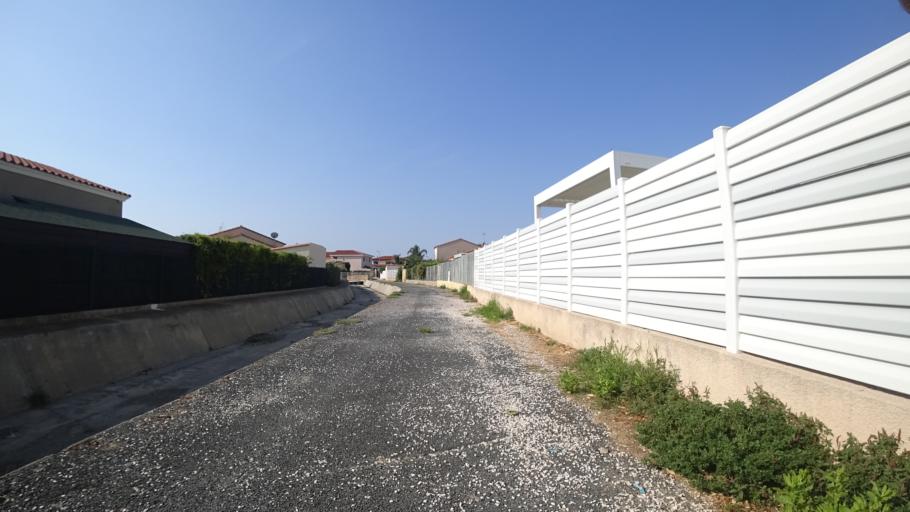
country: FR
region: Languedoc-Roussillon
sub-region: Departement des Pyrenees-Orientales
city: Saint-Laurent-de-la-Salanque
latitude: 42.7802
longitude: 2.9952
